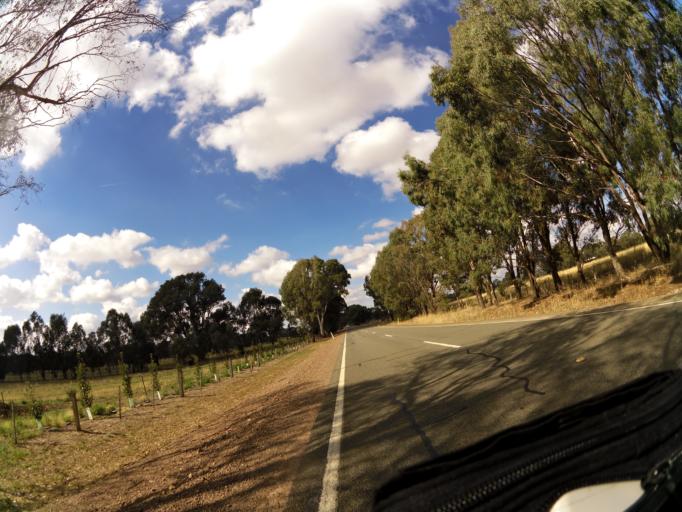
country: AU
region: Victoria
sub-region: Benalla
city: Benalla
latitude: -36.5917
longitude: 146.0096
